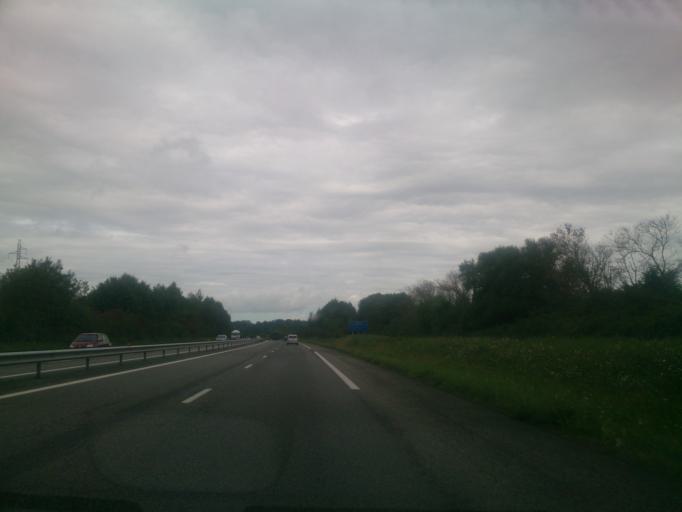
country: FR
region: Midi-Pyrenees
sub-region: Departement de la Haute-Garonne
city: Montrejeau
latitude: 43.0979
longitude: 0.4946
